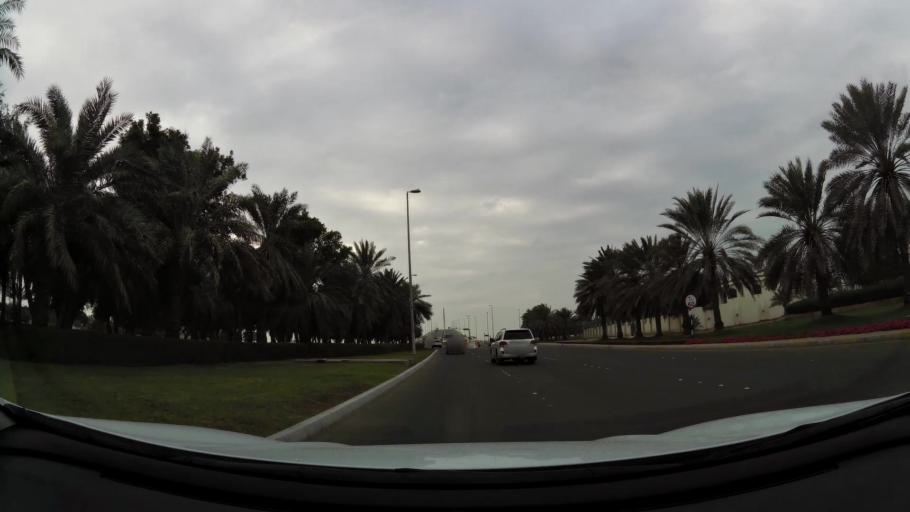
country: AE
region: Abu Dhabi
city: Abu Dhabi
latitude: 24.4319
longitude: 54.3727
